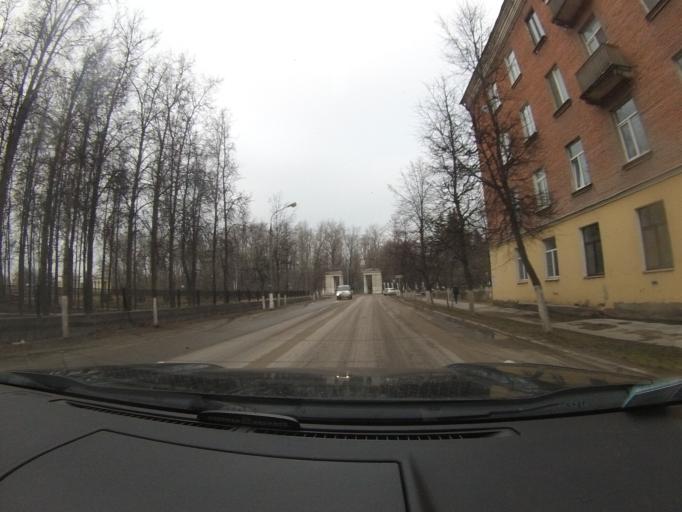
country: RU
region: Moskovskaya
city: Peski
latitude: 55.2522
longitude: 38.7575
